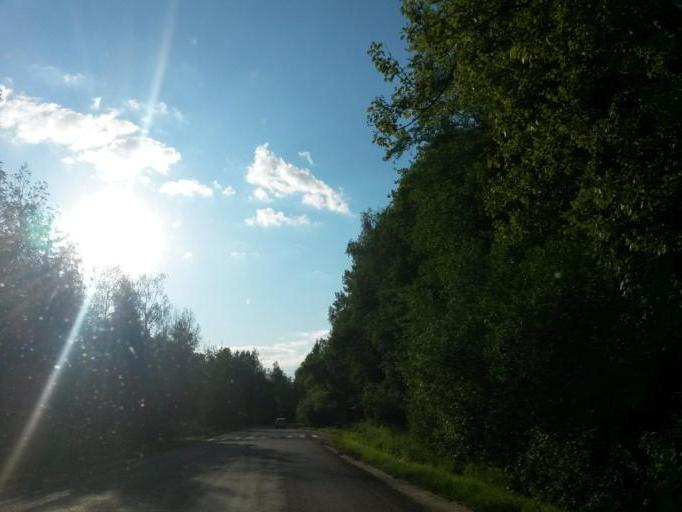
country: RU
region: Moskovskaya
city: Melikhovo
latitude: 55.2154
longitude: 37.6853
